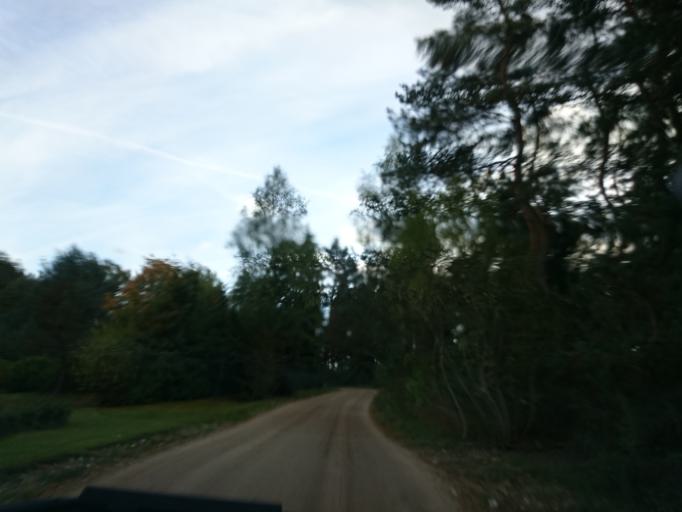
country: LV
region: Garkalne
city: Garkalne
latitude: 57.0511
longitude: 24.3770
